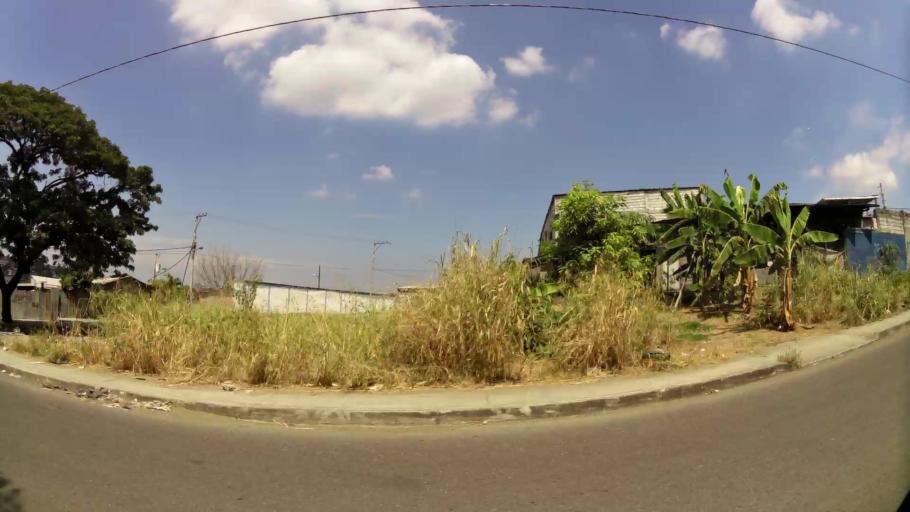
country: EC
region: Guayas
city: Guayaquil
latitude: -2.1173
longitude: -79.9246
